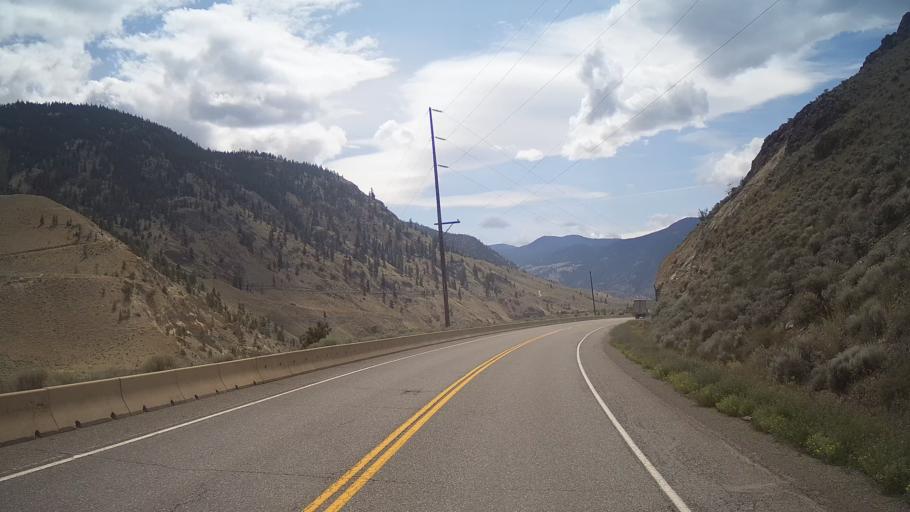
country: CA
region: British Columbia
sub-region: Thompson-Nicola Regional District
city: Ashcroft
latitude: 50.4679
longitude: -121.3002
